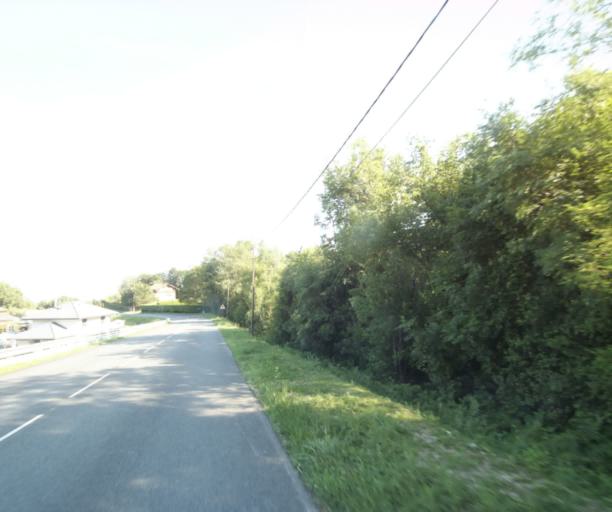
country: FR
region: Rhone-Alpes
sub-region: Departement de la Haute-Savoie
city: Lyaud
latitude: 46.3447
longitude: 6.5282
